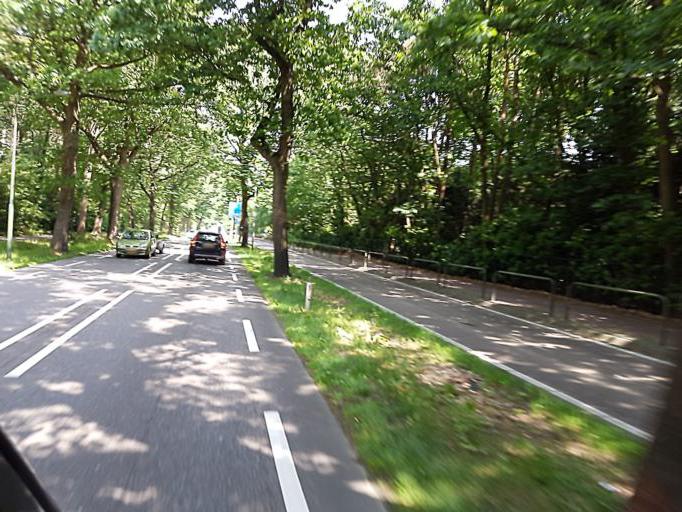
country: NL
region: North Brabant
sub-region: Gemeente Waalre
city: Waalre
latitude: 51.3886
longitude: 5.4734
